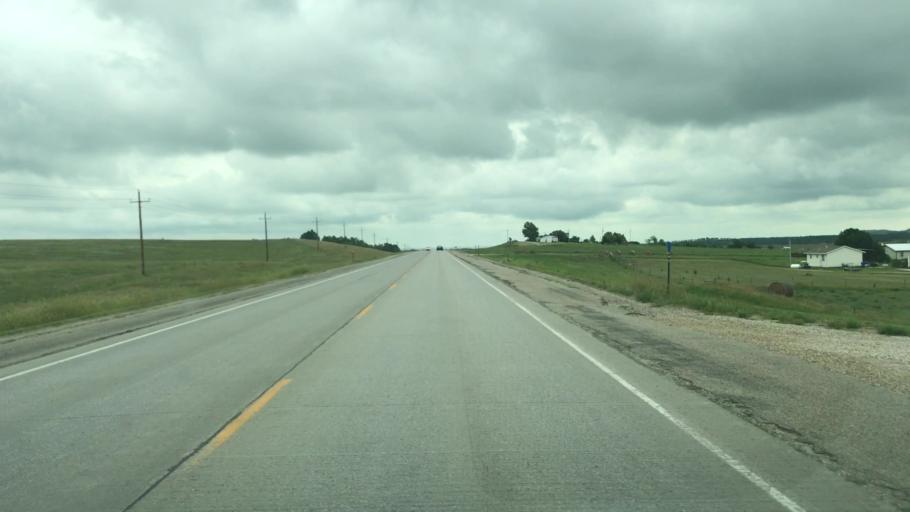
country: US
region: South Dakota
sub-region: Todd County
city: Mission
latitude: 43.3029
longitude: -100.6997
